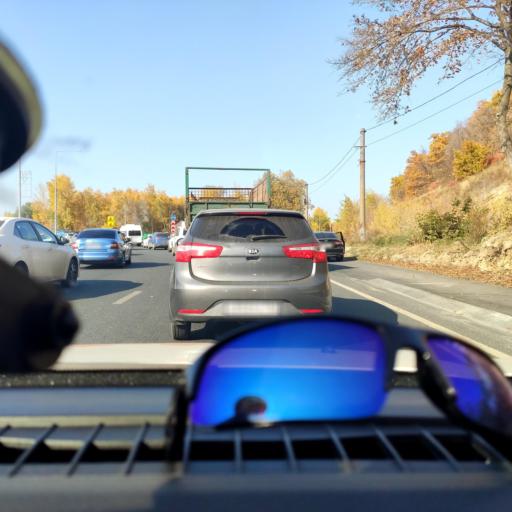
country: RU
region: Samara
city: Volzhskiy
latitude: 53.4087
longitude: 50.1428
